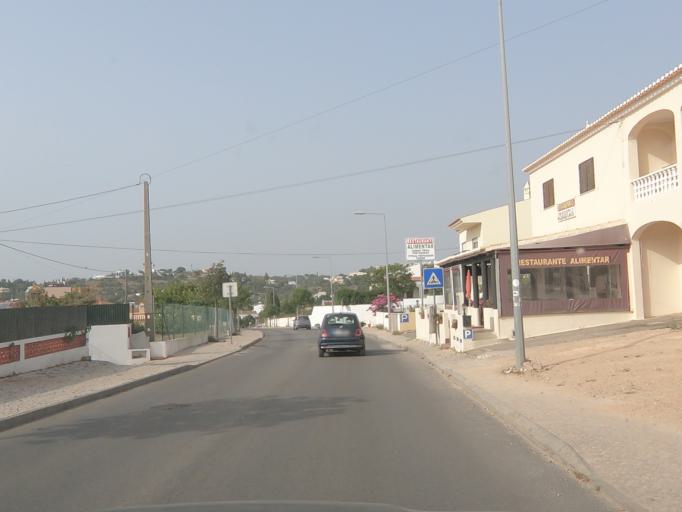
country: PT
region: Faro
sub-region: Albufeira
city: Guia
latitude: 37.0832
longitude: -8.2971
